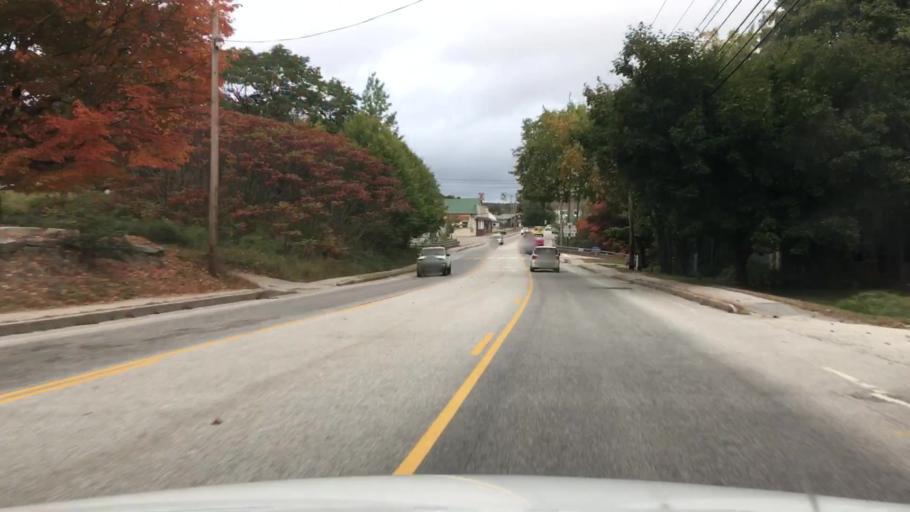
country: US
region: Maine
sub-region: Oxford County
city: Norway
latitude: 44.2051
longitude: -70.5316
